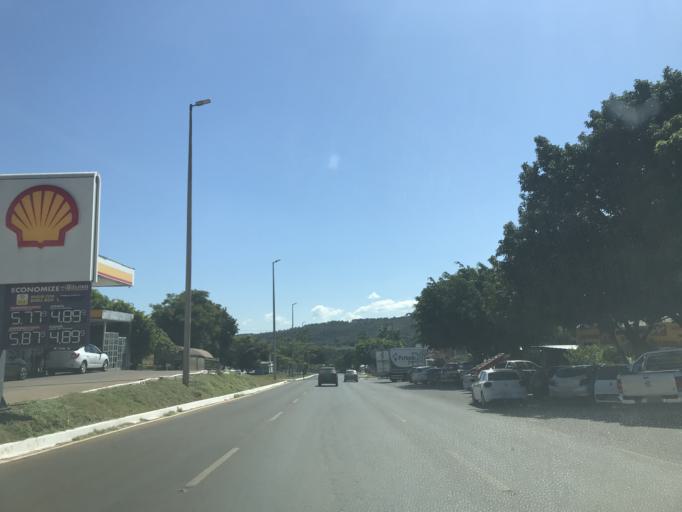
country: BR
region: Federal District
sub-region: Brasilia
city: Brasilia
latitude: -15.6470
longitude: -47.7861
